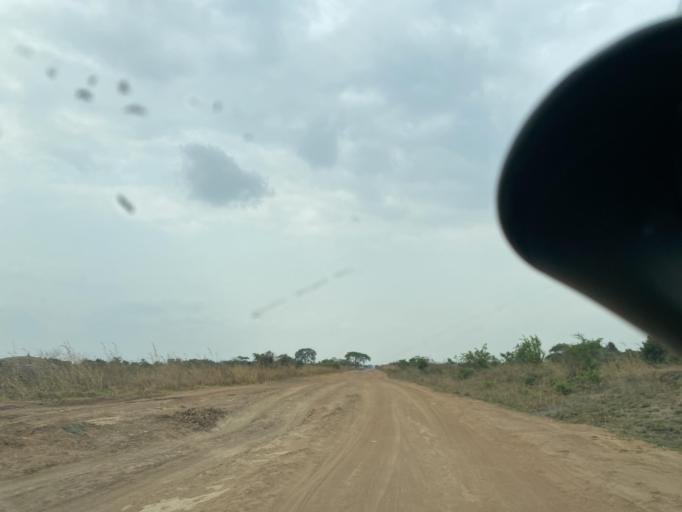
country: ZM
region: Lusaka
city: Lusaka
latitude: -15.2225
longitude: 28.3371
